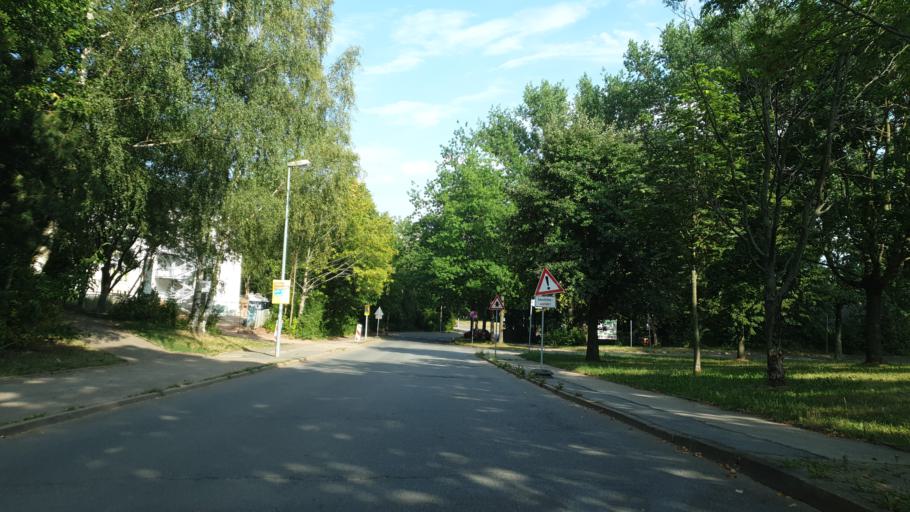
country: DE
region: Saxony
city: Neukirchen
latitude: 50.7916
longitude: 12.8861
